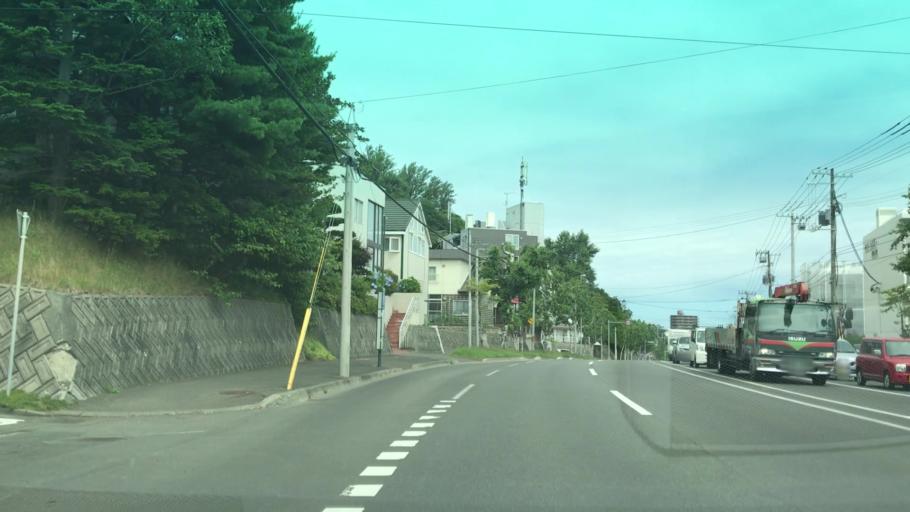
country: JP
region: Hokkaido
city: Sapporo
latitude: 43.0655
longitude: 141.2889
